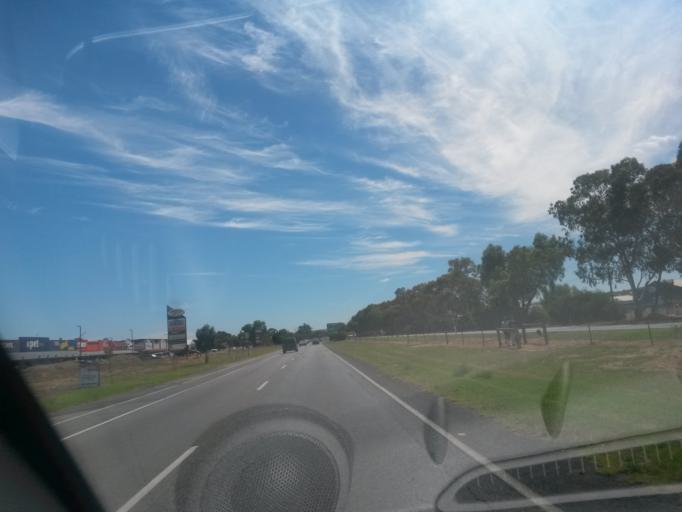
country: AU
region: South Australia
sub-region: Salisbury
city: Salisbury
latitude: -34.7965
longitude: 138.6427
